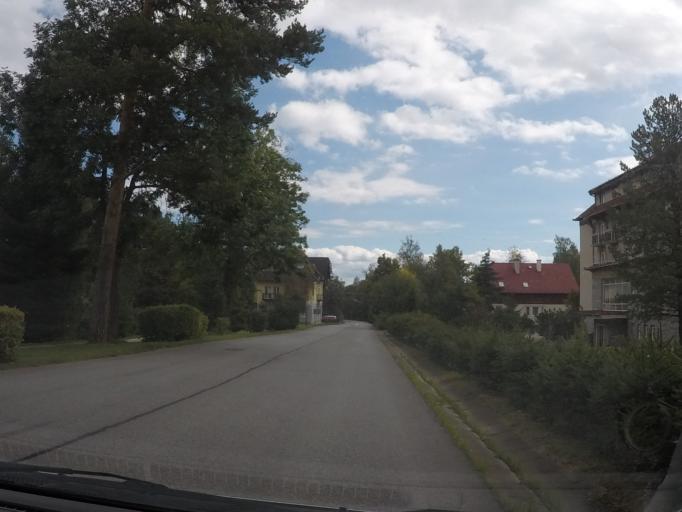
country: SK
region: Presovsky
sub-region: Okres Poprad
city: Nova Lesna
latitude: 49.1618
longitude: 20.2864
